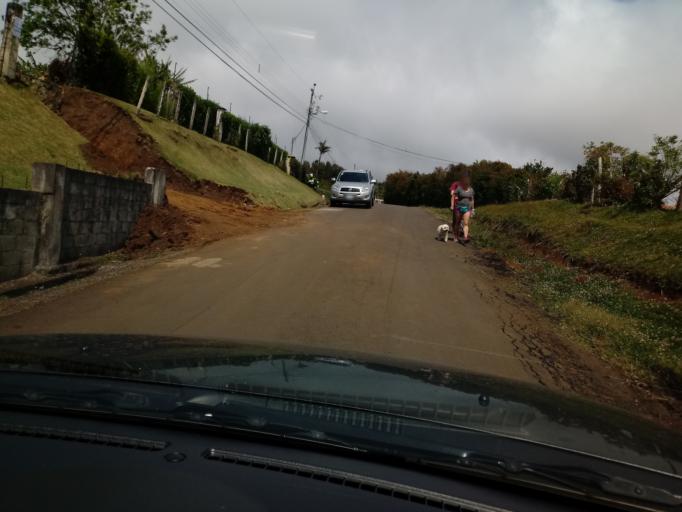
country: CR
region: Heredia
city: Angeles
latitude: 10.0297
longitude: -84.0335
